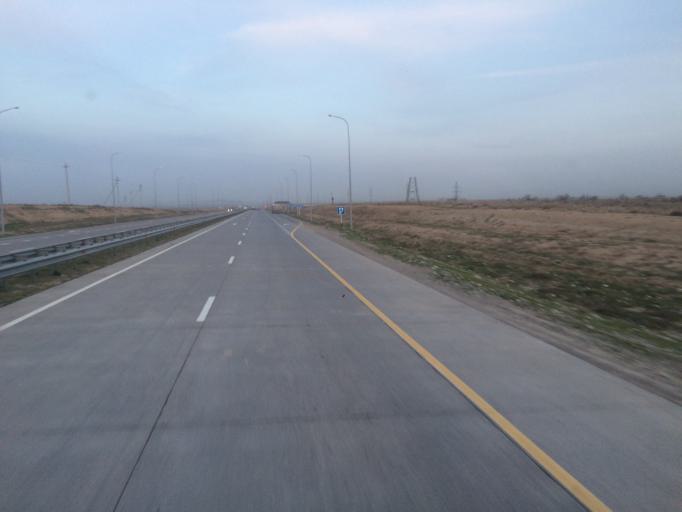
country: KZ
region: Ongtustik Qazaqstan
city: Shymkent
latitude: 42.4528
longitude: 69.6263
